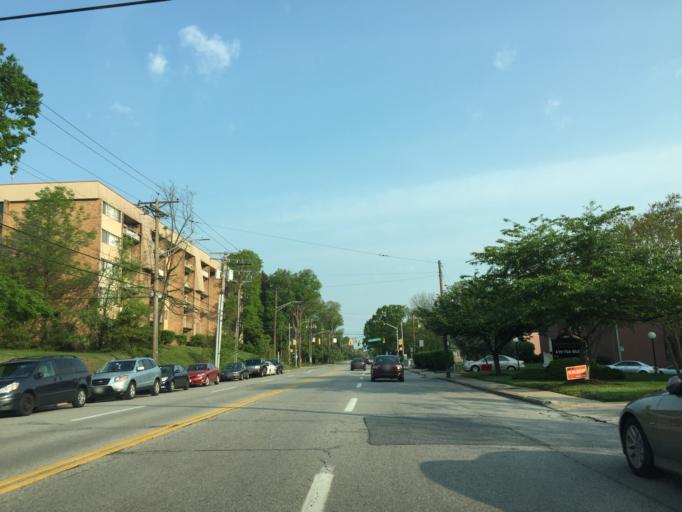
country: US
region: Maryland
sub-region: Baltimore County
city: Pikesville
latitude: 39.3640
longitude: -76.7017
